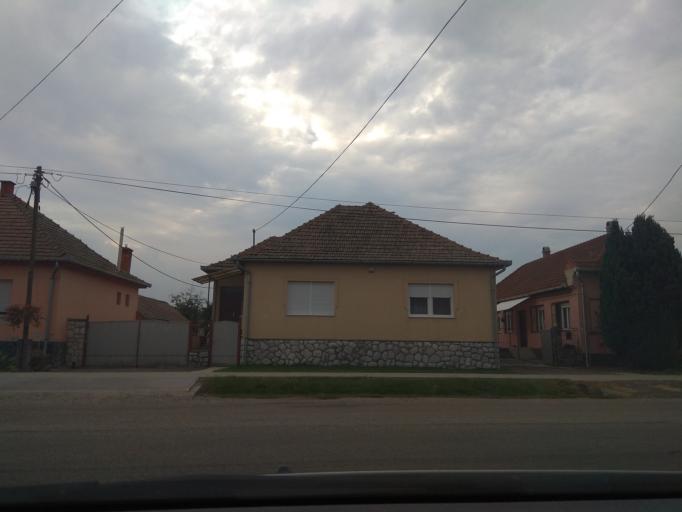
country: HU
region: Heves
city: Egerszalok
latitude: 47.8697
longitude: 20.3227
